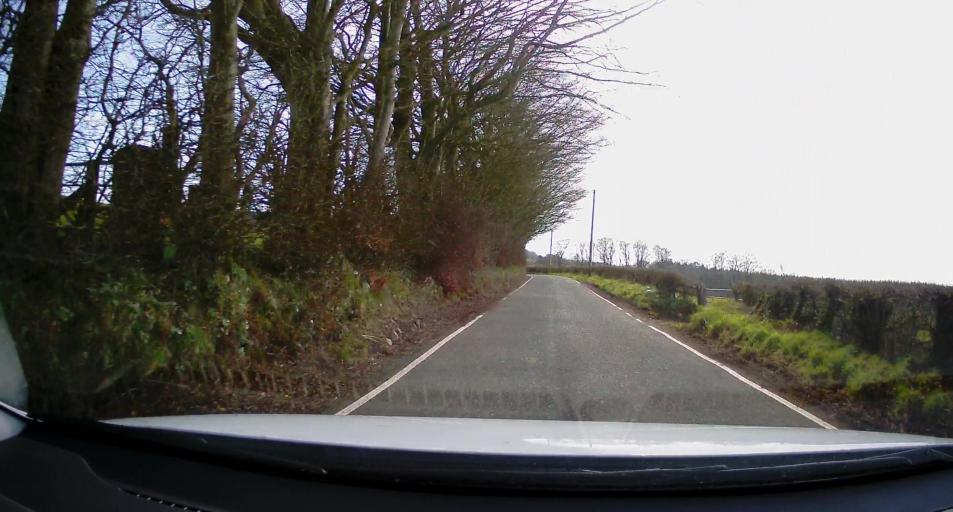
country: GB
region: Wales
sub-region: County of Ceredigion
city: Lledrod
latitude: 52.2665
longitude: -4.0709
